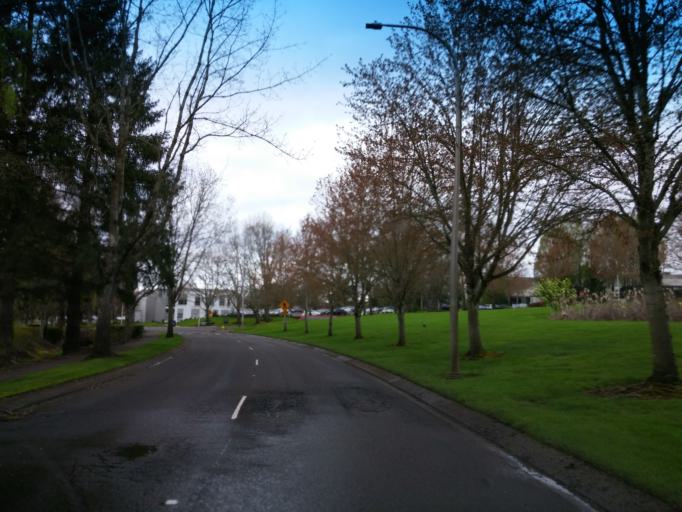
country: US
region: Oregon
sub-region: Washington County
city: Oak Hills
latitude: 45.5267
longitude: -122.8323
